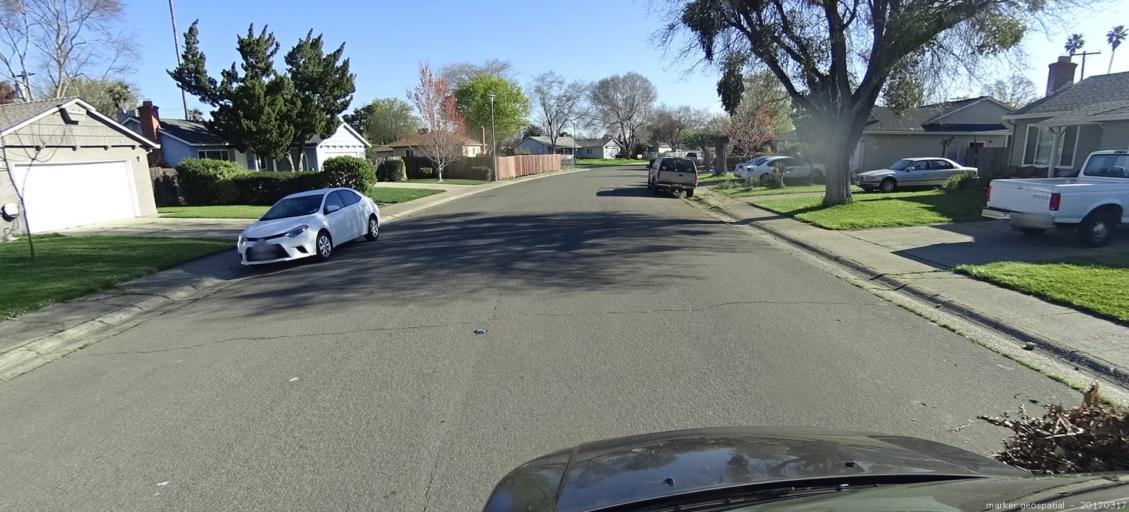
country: US
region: California
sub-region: Sacramento County
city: Parkway
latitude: 38.4876
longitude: -121.5035
